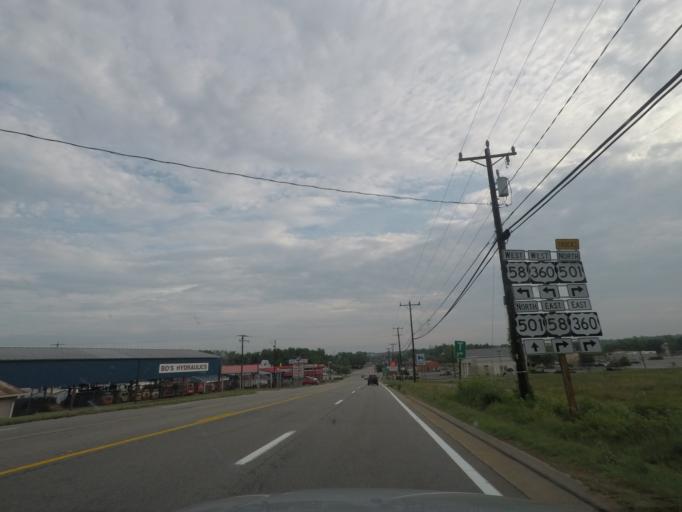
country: US
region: Virginia
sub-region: Halifax County
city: South Boston
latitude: 36.6849
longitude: -78.8994
